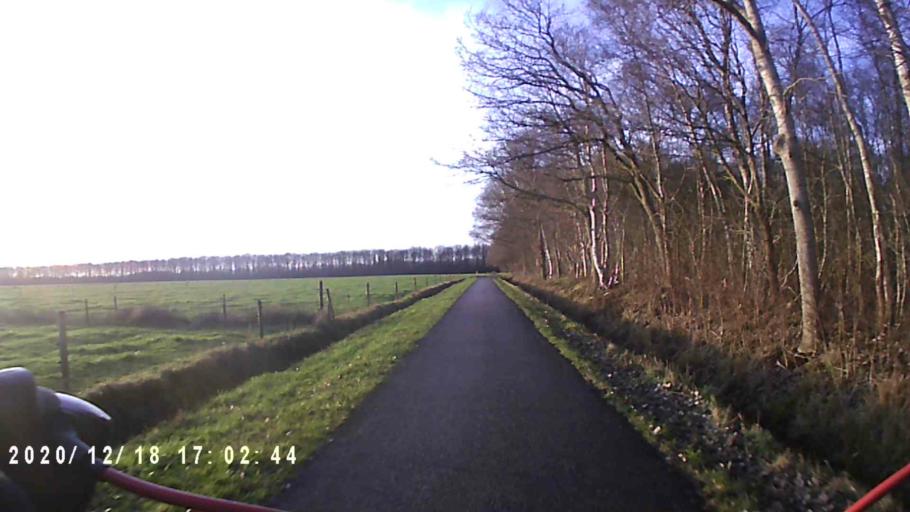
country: NL
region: Drenthe
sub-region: Gemeente Tynaarlo
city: Tynaarlo
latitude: 53.0637
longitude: 6.6341
